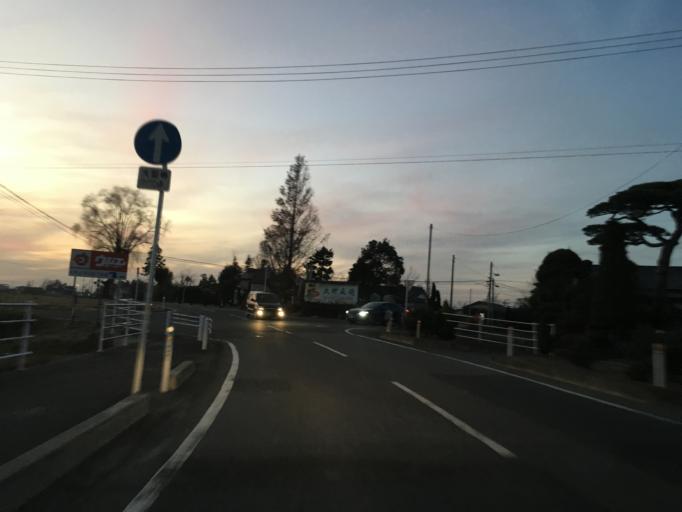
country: JP
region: Miyagi
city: Wakuya
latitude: 38.7126
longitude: 141.2329
